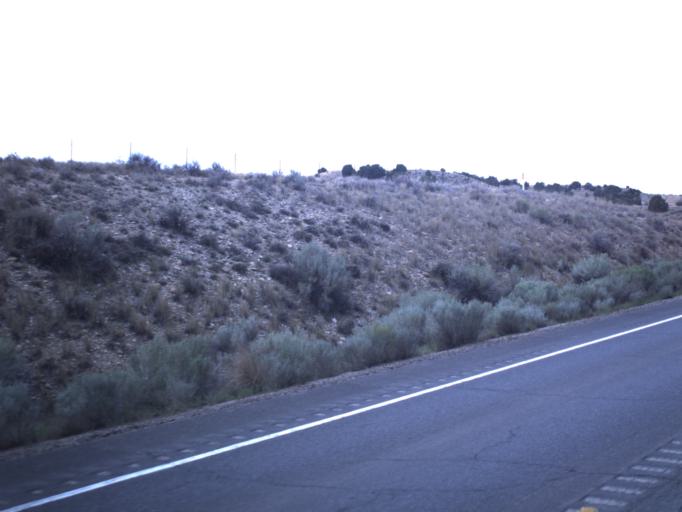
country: US
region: Utah
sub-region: Duchesne County
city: Duchesne
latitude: 40.1659
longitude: -110.2891
